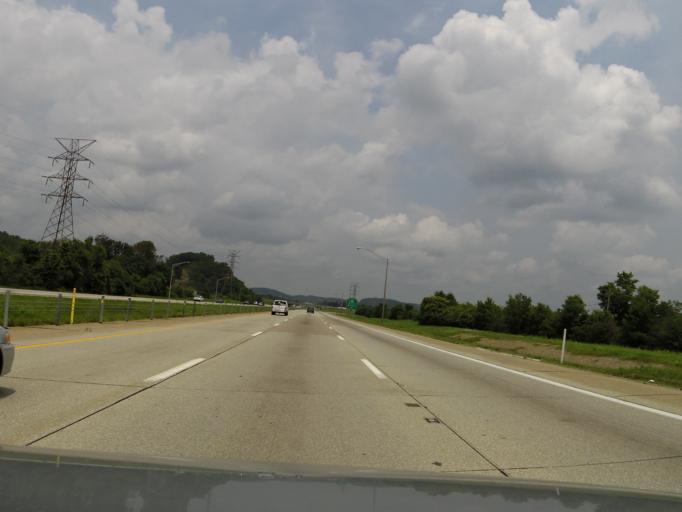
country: US
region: Kentucky
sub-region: Bullitt County
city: Shepherdsville
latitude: 37.9178
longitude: -85.6870
